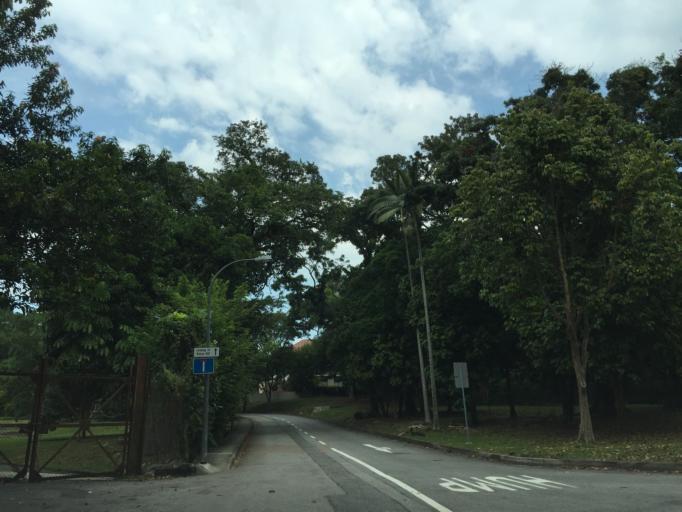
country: SG
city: Singapore
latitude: 1.3066
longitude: 103.8080
